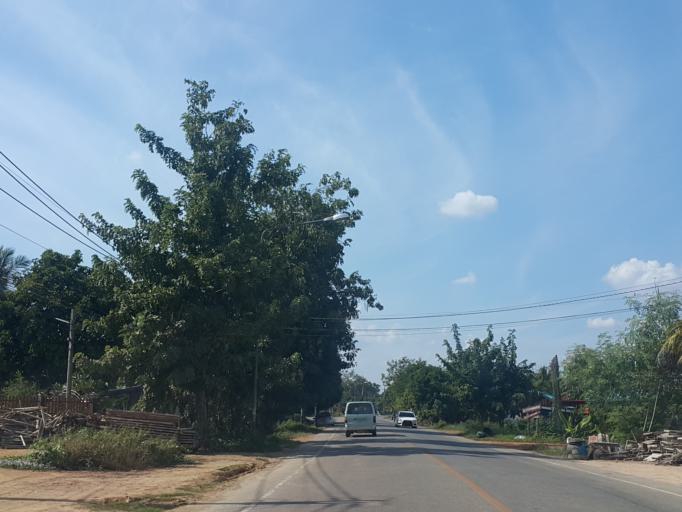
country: TH
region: Sukhothai
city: Sawankhalok
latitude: 17.2929
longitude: 99.8306
